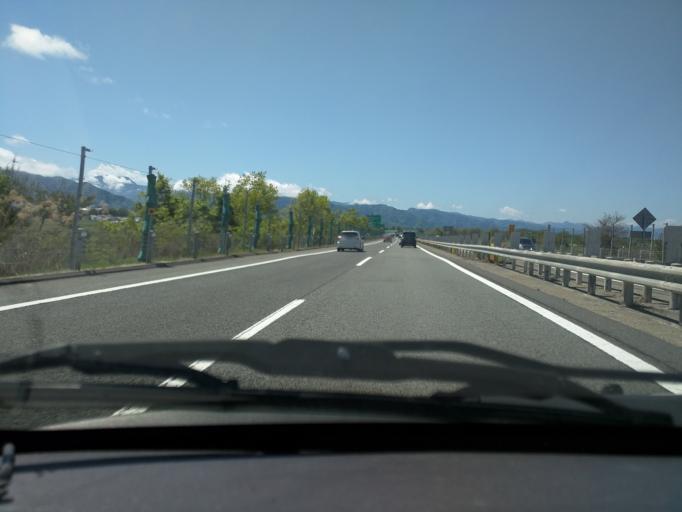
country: JP
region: Nagano
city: Nakano
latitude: 36.7219
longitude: 138.3145
